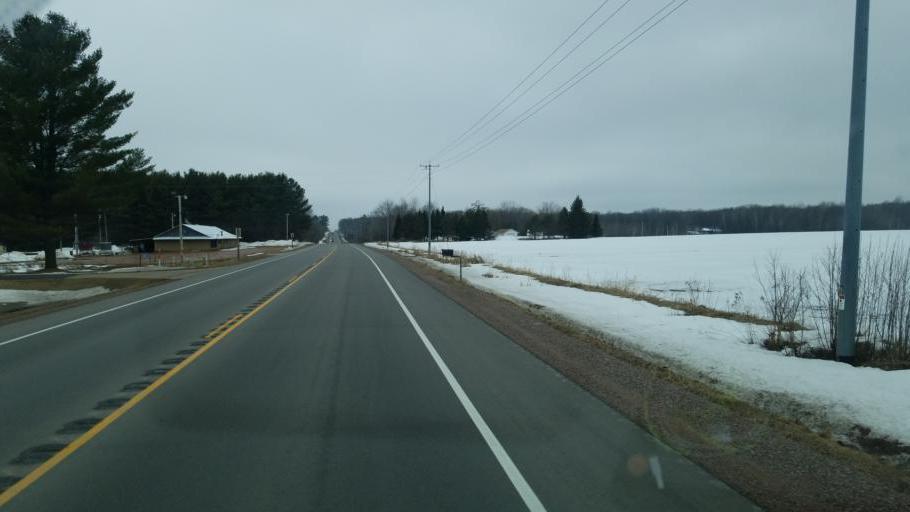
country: US
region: Wisconsin
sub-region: Wood County
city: Marshfield
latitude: 44.6563
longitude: -90.2479
